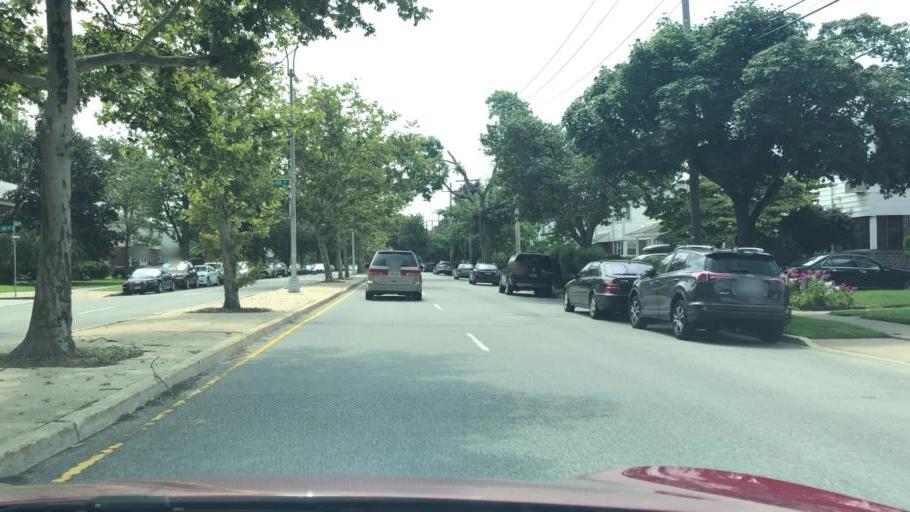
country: US
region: New York
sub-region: Nassau County
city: Bellerose Terrace
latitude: 40.7431
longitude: -73.7594
